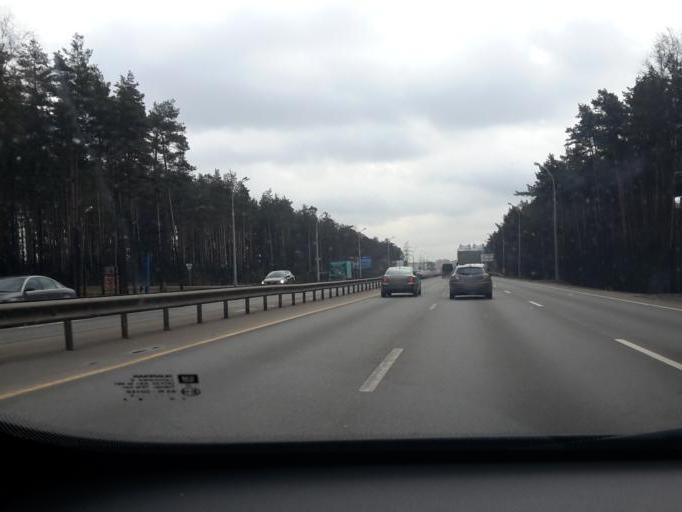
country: BY
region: Minsk
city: Borovlyany
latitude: 53.9490
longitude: 27.6567
